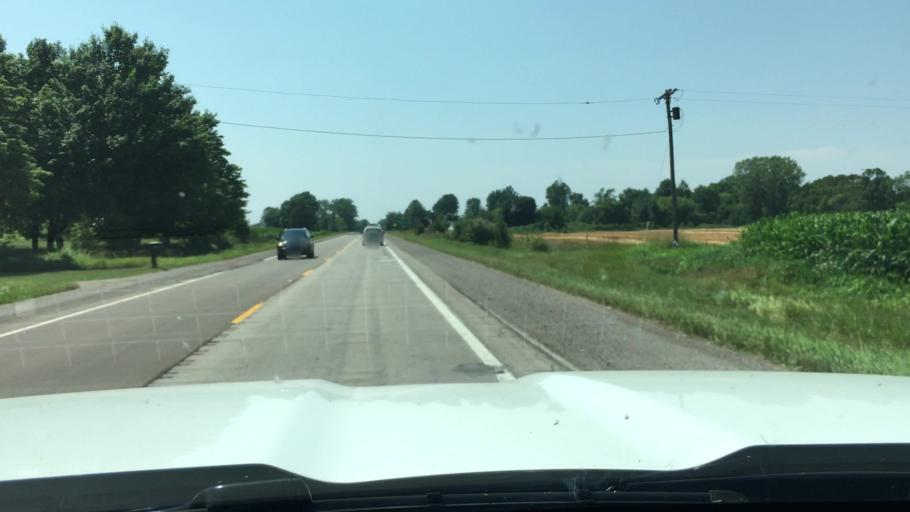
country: US
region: Michigan
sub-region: Saginaw County
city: Chesaning
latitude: 43.1868
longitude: -84.2225
